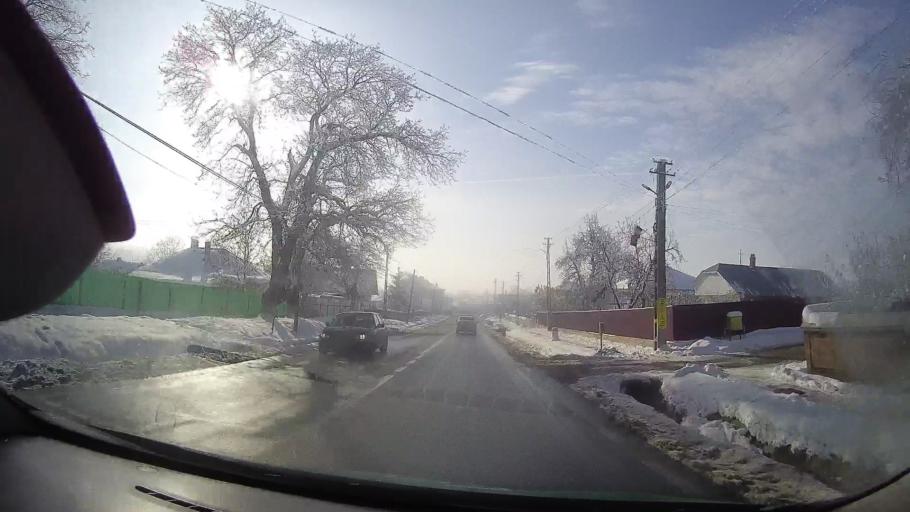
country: RO
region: Iasi
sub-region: Comuna Motca
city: Motca
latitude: 47.2412
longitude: 26.6073
